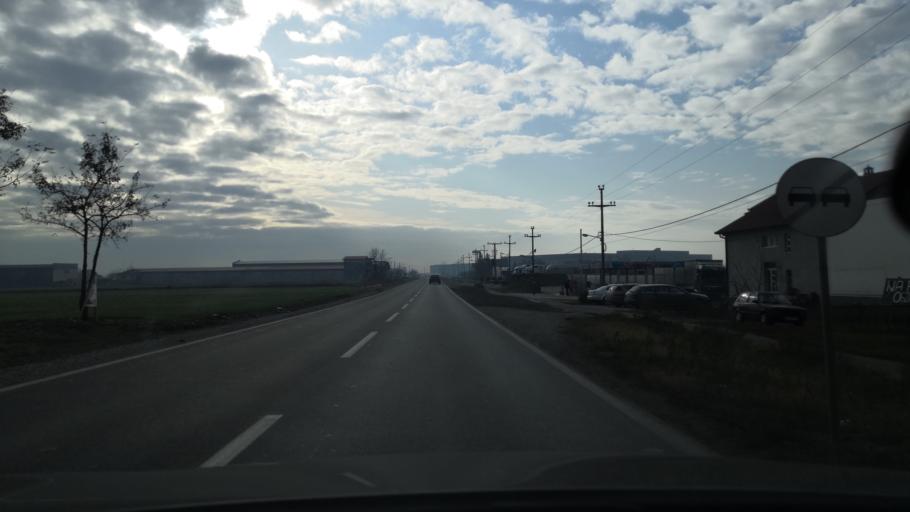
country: RS
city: Ugrinovci
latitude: 44.8593
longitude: 20.2050
